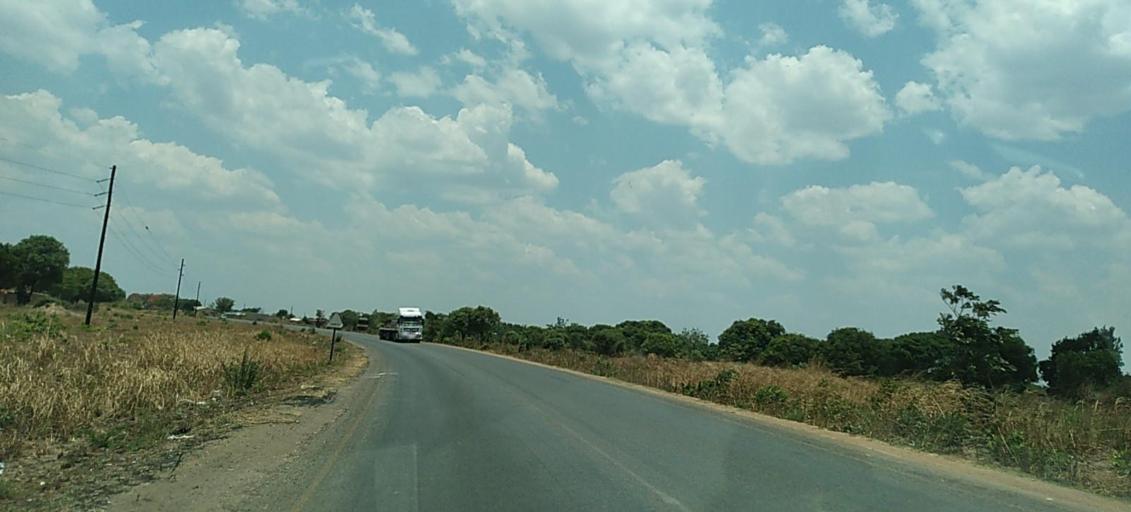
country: ZM
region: Central
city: Kapiri Mposhi
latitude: -13.8907
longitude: 28.6507
